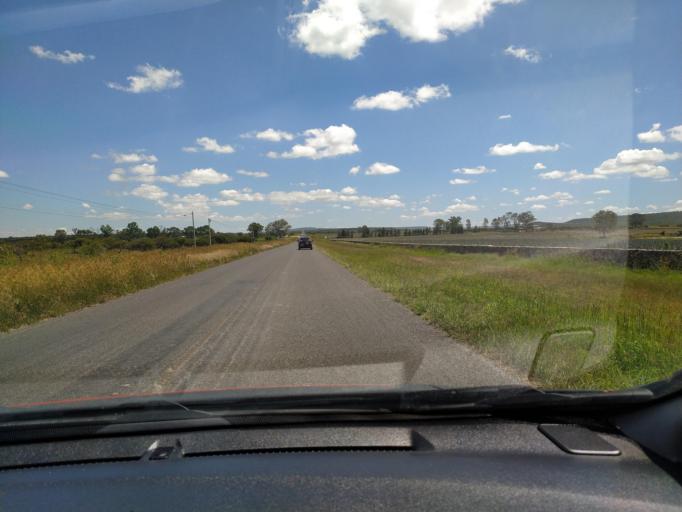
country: MX
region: Jalisco
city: San Diego de Alejandria
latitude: 21.0049
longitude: -102.0698
